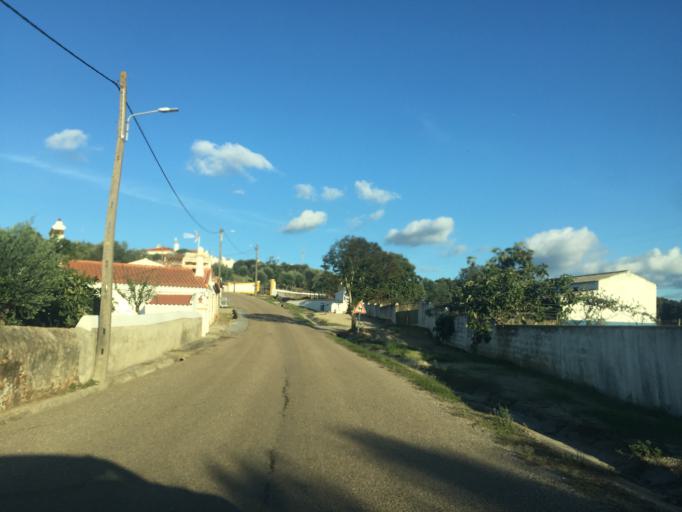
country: PT
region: Portalegre
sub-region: Alter do Chao
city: Alter do Chao
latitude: 39.1868
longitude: -7.6274
